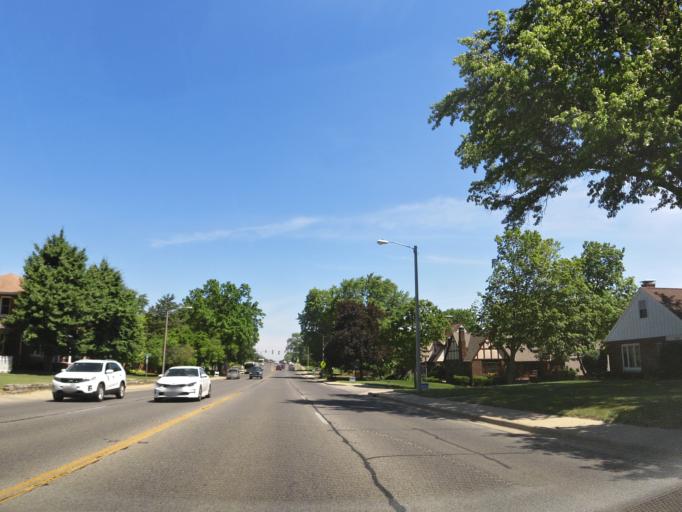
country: US
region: Illinois
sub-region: Vermilion County
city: Danville
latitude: 40.1575
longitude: -87.6304
